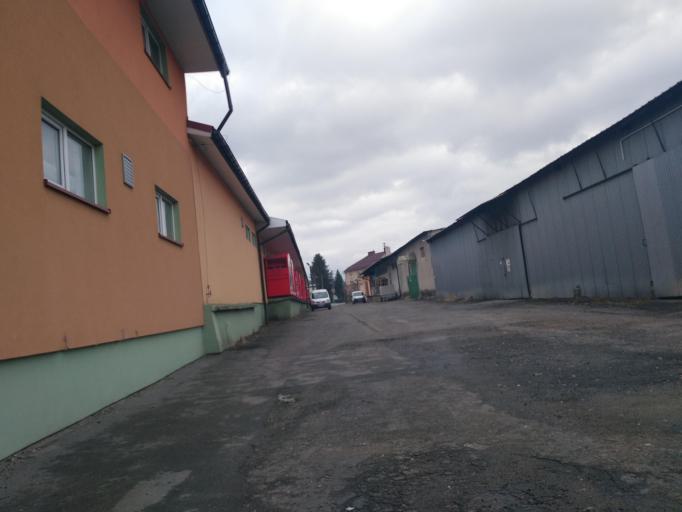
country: PL
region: Subcarpathian Voivodeship
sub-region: Powiat strzyzowski
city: Strzyzow
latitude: 49.8685
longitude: 21.8028
